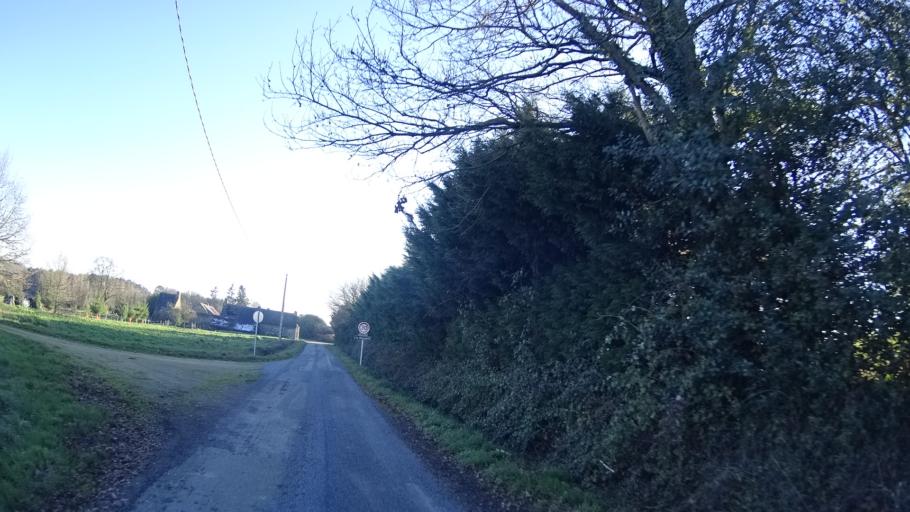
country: FR
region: Brittany
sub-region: Departement du Morbihan
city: Saint-Jacut-les-Pins
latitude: 47.6702
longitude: -2.1945
